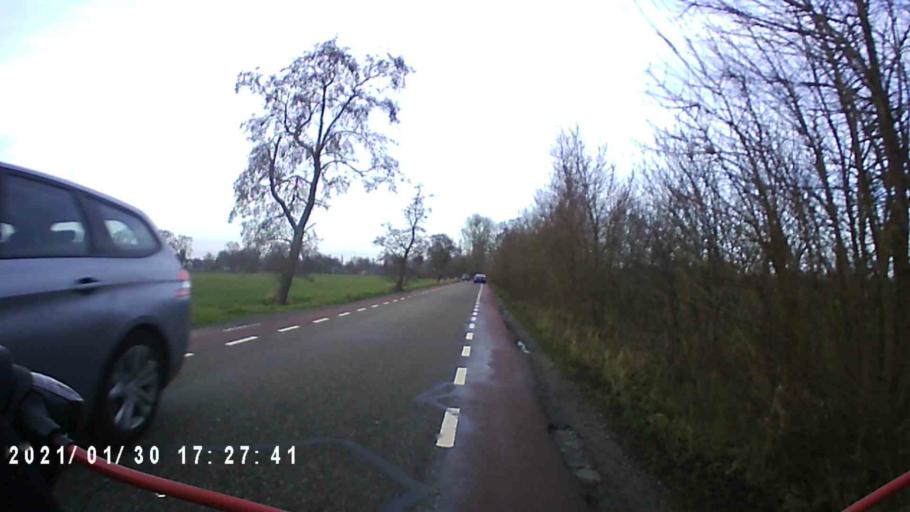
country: NL
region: Groningen
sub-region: Gemeente Zuidhorn
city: Grijpskerk
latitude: 53.2166
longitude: 6.3456
